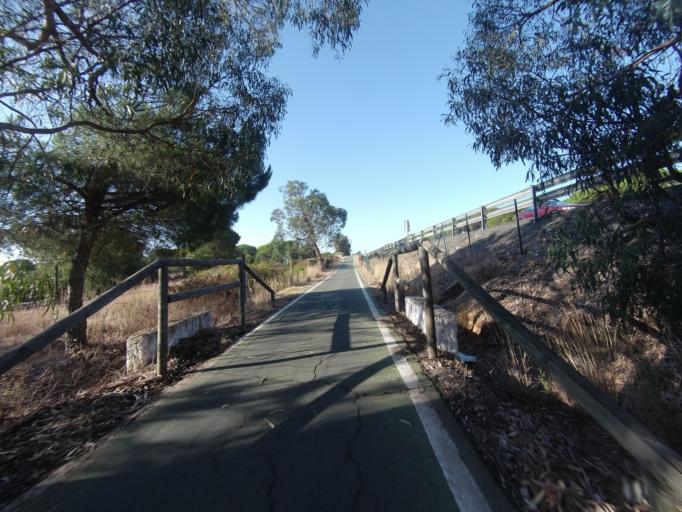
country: ES
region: Andalusia
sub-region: Provincia de Huelva
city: Aljaraque
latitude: 37.2439
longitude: -7.0182
